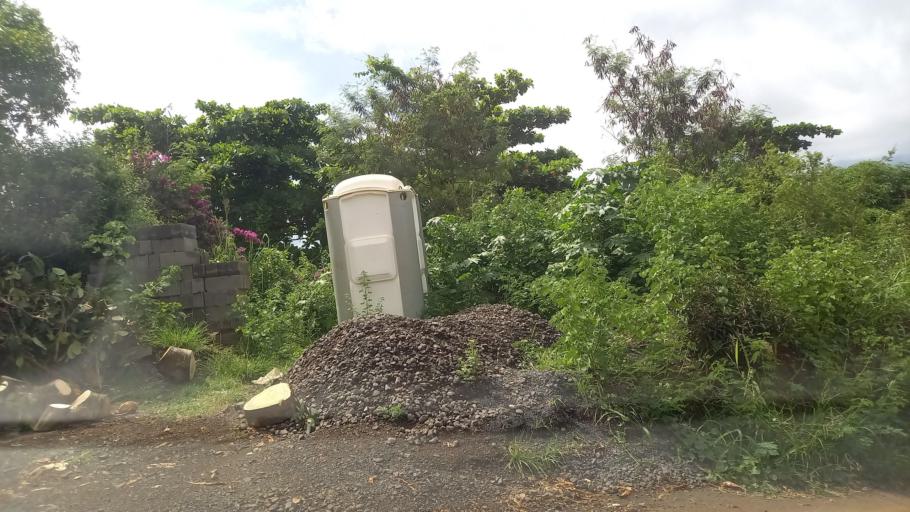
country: YT
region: Sada
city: Sada
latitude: -12.8495
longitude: 45.1062
